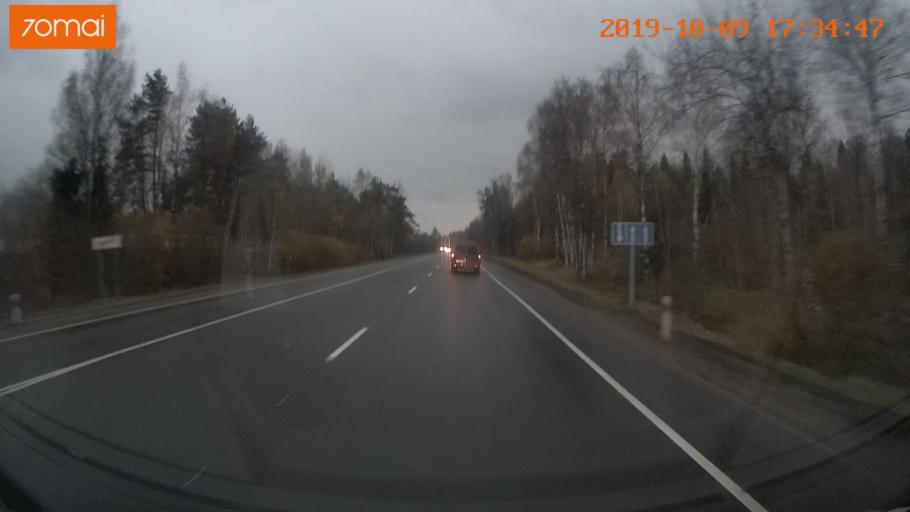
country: RU
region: Ivanovo
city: Bogorodskoye
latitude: 57.1032
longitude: 41.0086
